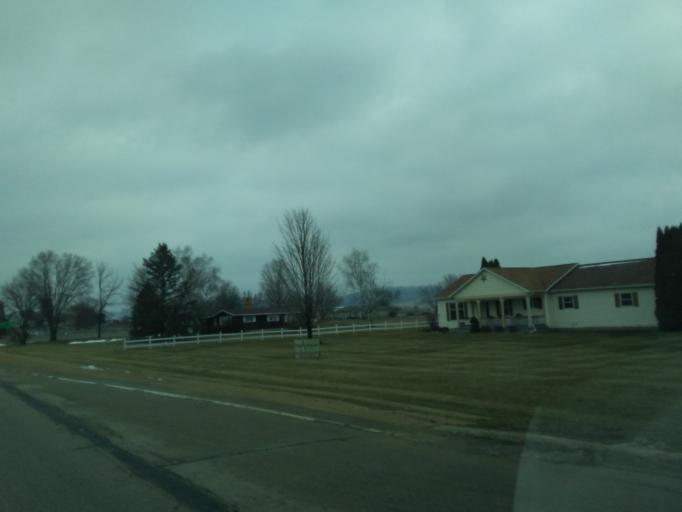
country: US
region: Wisconsin
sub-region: Richland County
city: Richland Center
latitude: 43.2249
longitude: -90.2915
